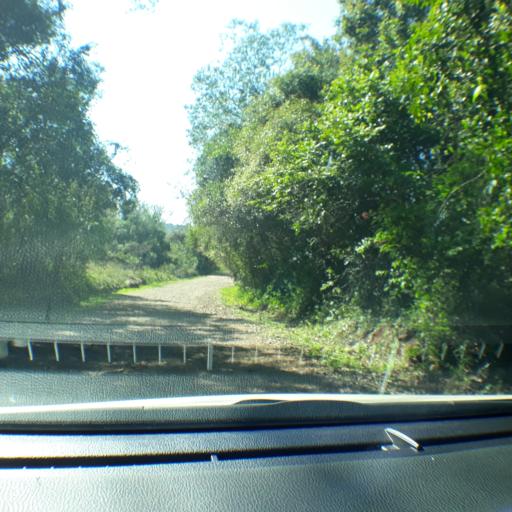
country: AR
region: Misiones
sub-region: Departamento de San Ignacio
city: San Ignacio
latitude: -27.2822
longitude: -55.5623
